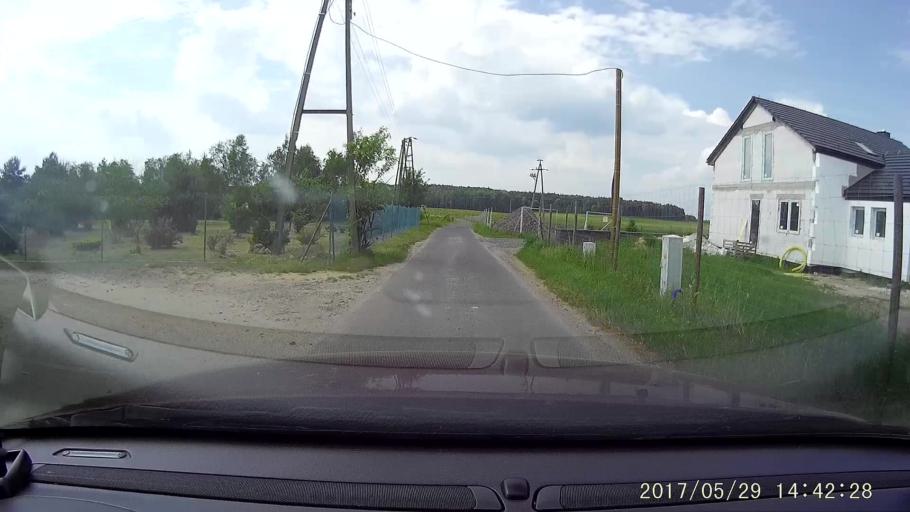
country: PL
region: Lower Silesian Voivodeship
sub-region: Powiat zgorzelecki
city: Wegliniec
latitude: 51.2356
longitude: 15.1995
